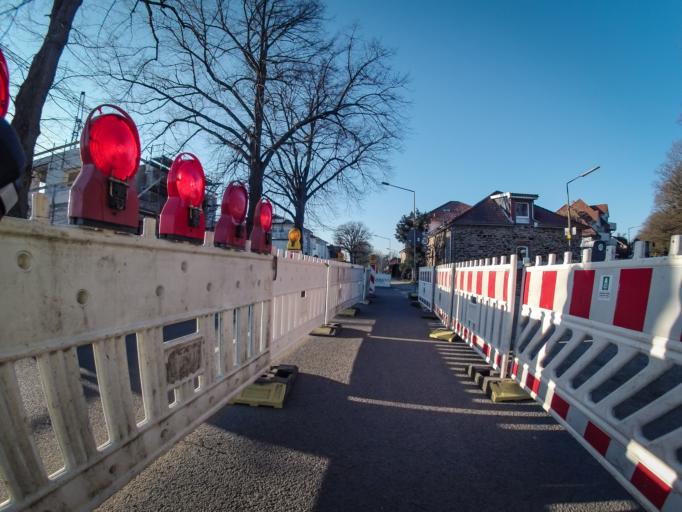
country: DE
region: Lower Saxony
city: Wallenhorst
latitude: 52.3171
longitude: 8.0032
